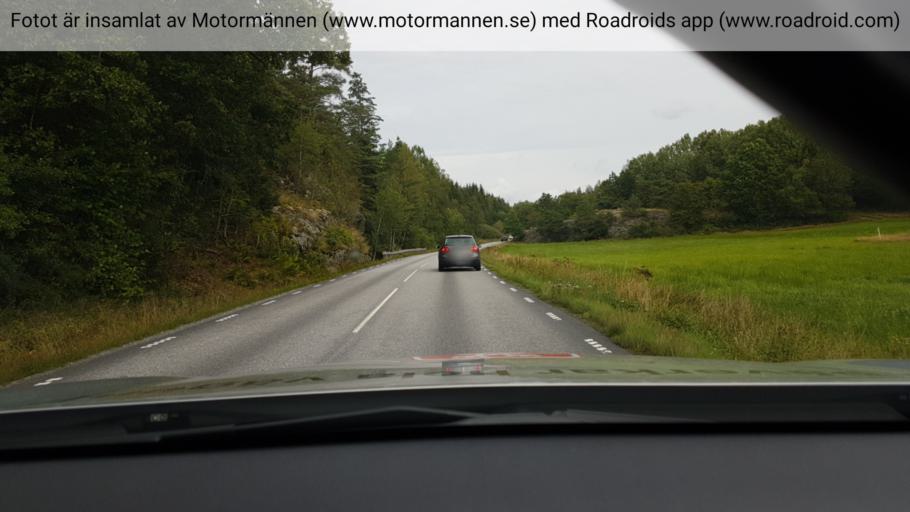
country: SE
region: Vaestra Goetaland
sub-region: Lysekils Kommun
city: Lysekil
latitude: 58.2678
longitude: 11.5367
